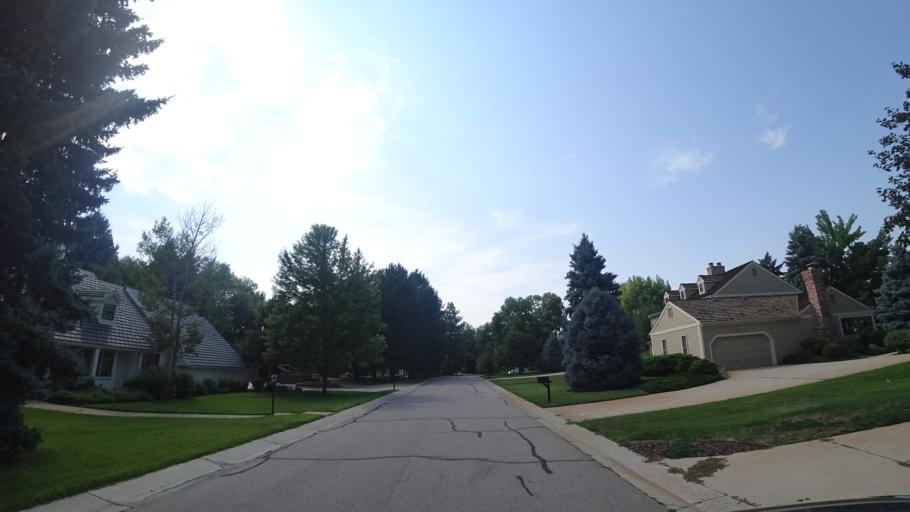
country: US
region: Colorado
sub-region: Arapahoe County
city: Greenwood Village
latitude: 39.6117
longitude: -104.9676
